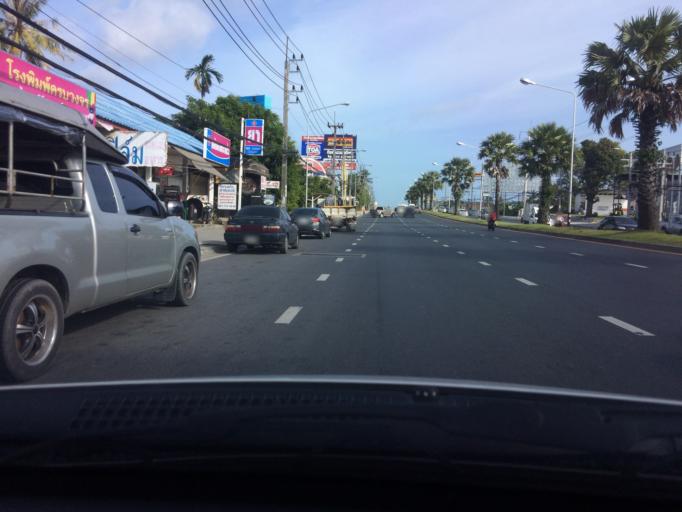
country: TH
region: Phuket
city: Ban Ko Kaeo
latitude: 7.9594
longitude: 98.3833
